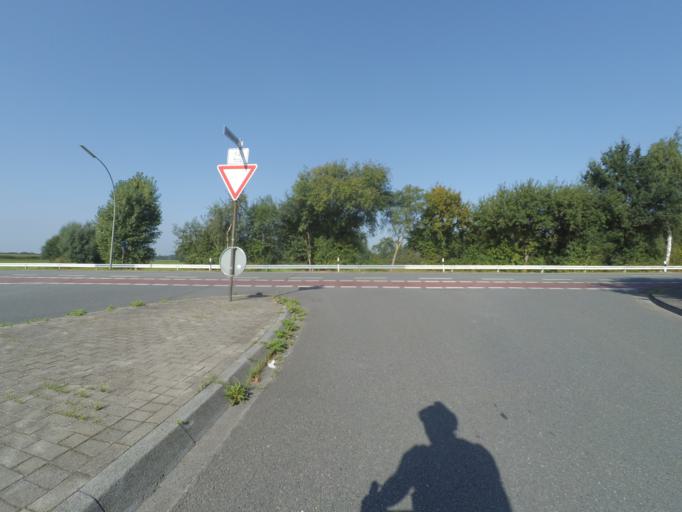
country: DE
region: North Rhine-Westphalia
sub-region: Regierungsbezirk Munster
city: Steinfurt
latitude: 52.1375
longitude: 7.3233
